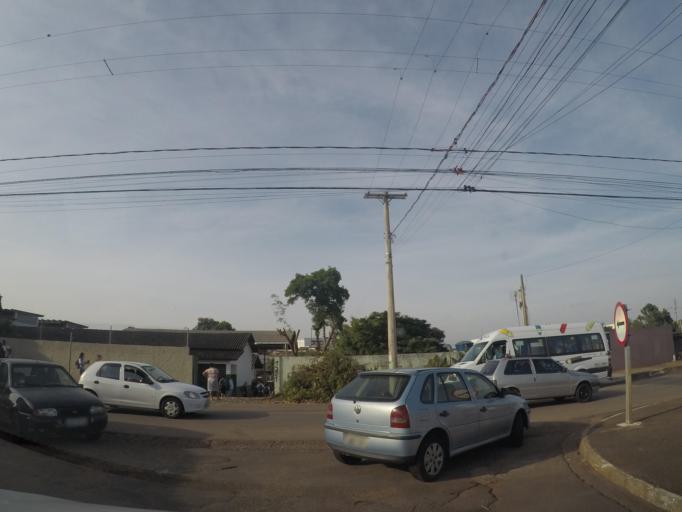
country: BR
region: Sao Paulo
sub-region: Hortolandia
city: Hortolandia
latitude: -22.8258
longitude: -47.1901
